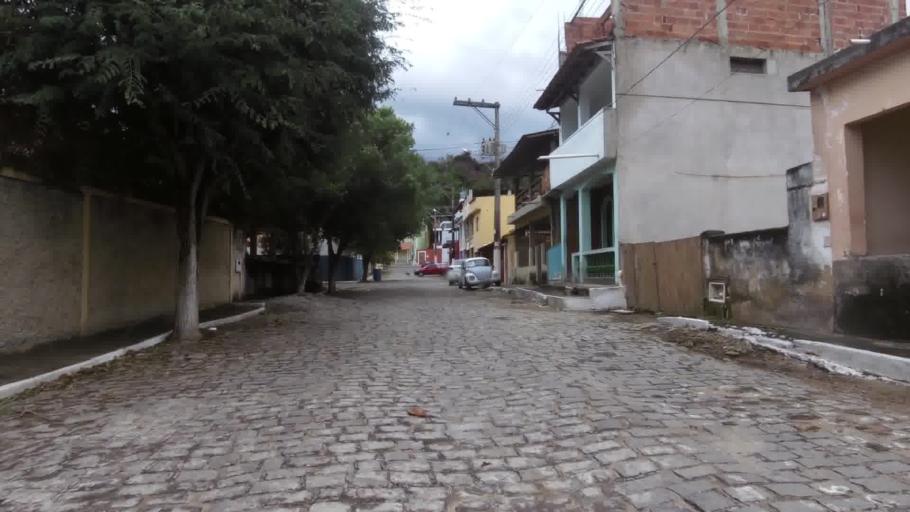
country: BR
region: Espirito Santo
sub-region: Marataizes
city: Marataizes
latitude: -21.0478
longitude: -40.8319
